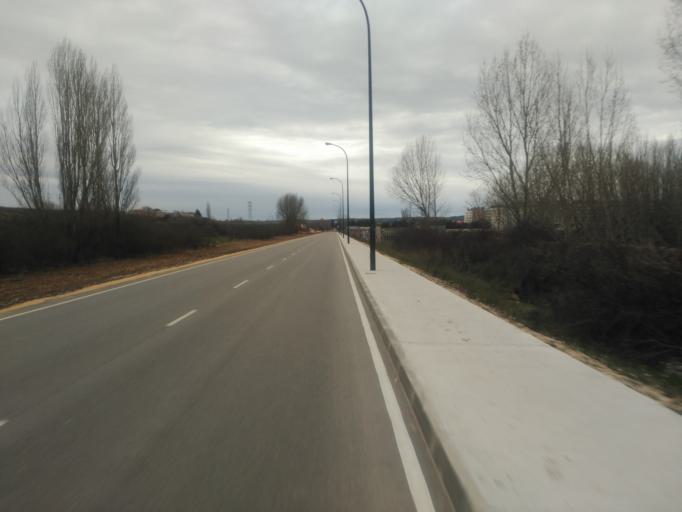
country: ES
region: Castille and Leon
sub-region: Provincia de Burgos
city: Villagonzalo-Pedernales
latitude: 42.3362
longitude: -3.7275
